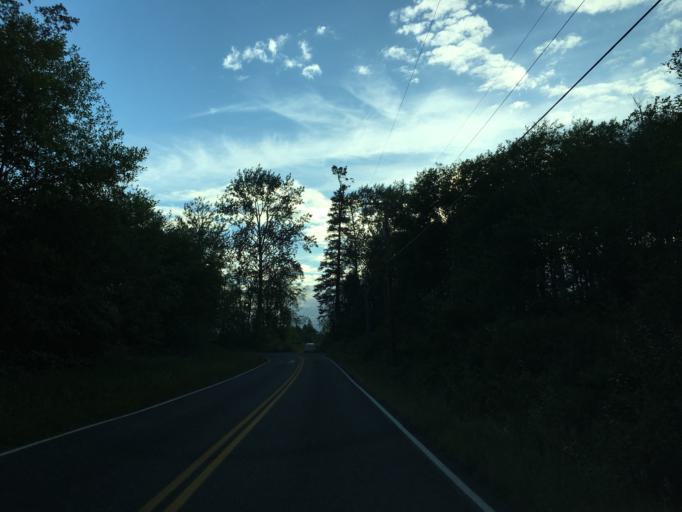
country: US
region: Washington
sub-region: Whatcom County
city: Birch Bay
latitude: 48.9440
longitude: -122.8015
